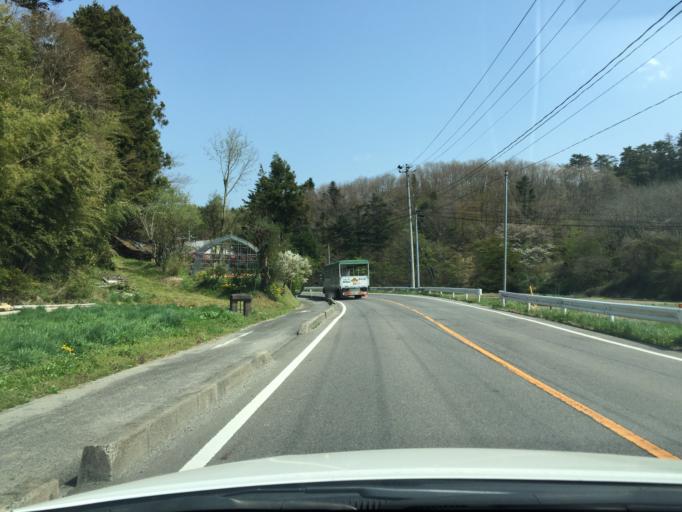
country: JP
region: Fukushima
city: Funehikimachi-funehiki
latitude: 37.4579
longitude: 140.7199
